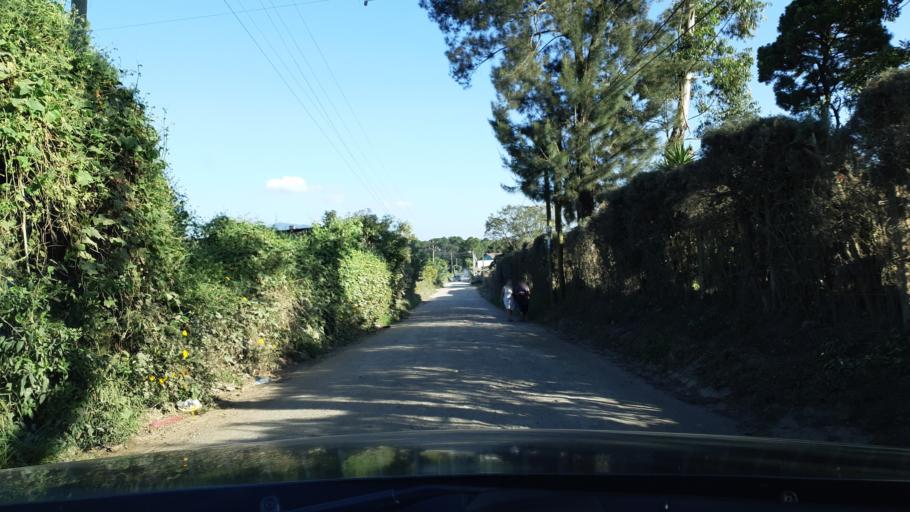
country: GT
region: Chimaltenango
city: El Tejar
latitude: 14.6382
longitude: -90.8034
